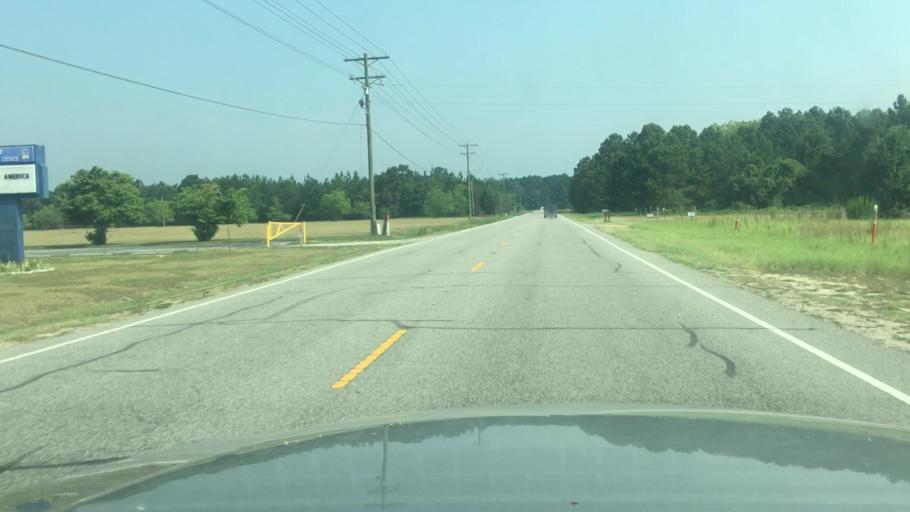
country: US
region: North Carolina
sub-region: Cumberland County
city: Hope Mills
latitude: 34.9080
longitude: -78.9039
